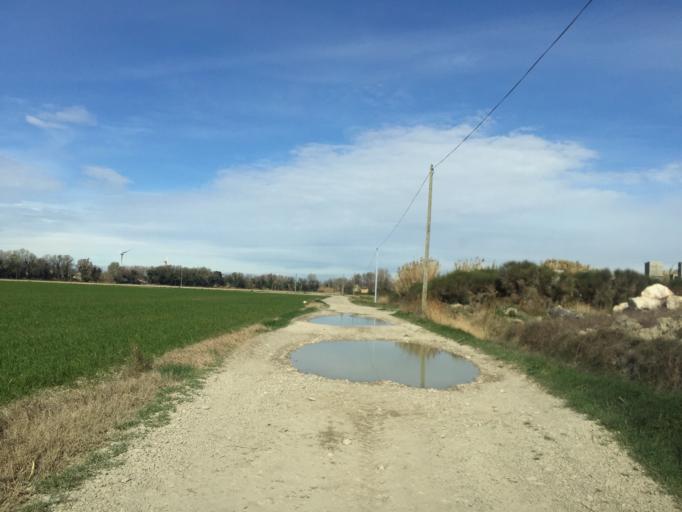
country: FR
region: Provence-Alpes-Cote d'Azur
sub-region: Departement du Vaucluse
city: Caderousse
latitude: 44.1411
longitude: 4.7378
